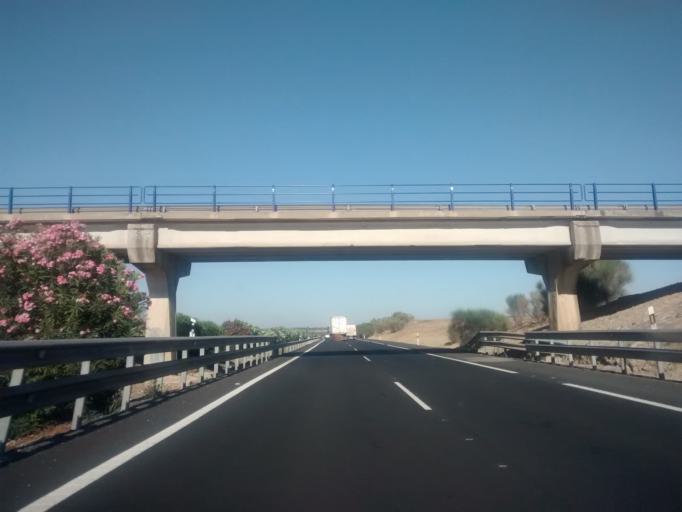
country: ES
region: Andalusia
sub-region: Provincia de Huelva
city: Bonares
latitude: 37.3412
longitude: -6.6941
